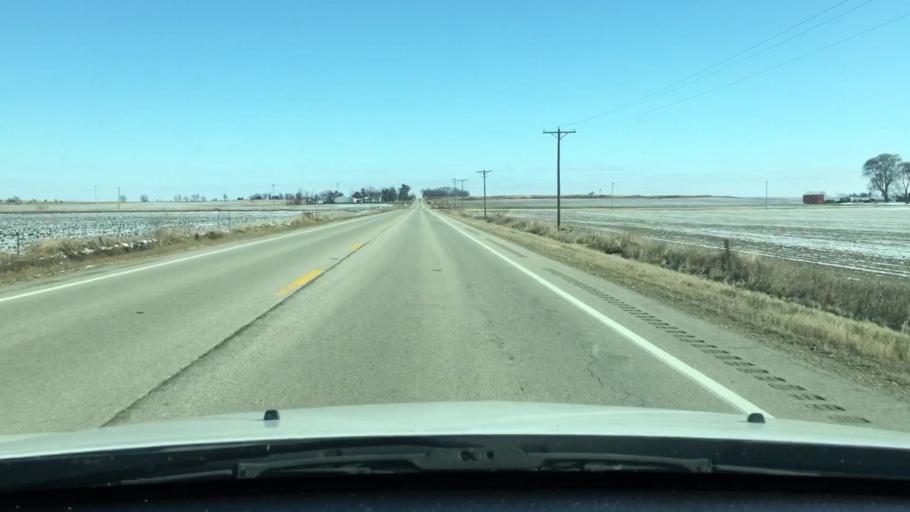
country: US
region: Illinois
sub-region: DeKalb County
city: Malta
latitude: 42.0008
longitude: -88.9207
